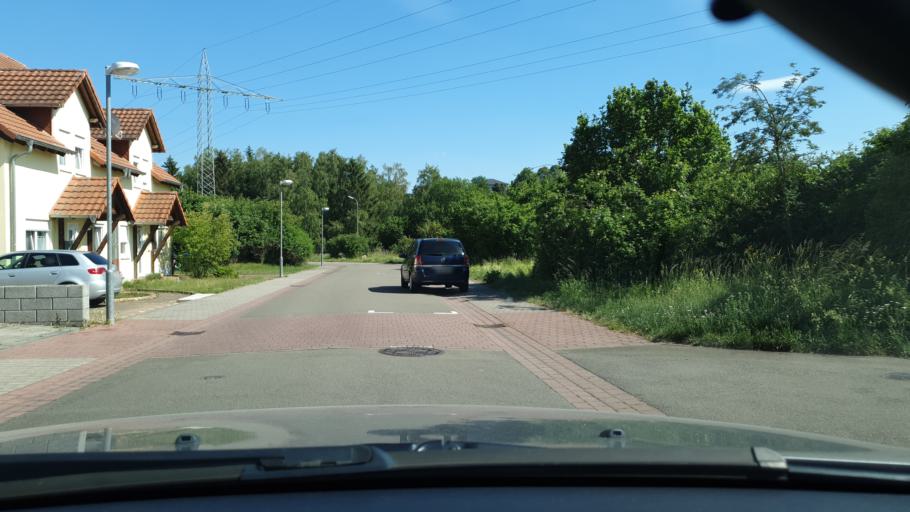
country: DE
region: Rheinland-Pfalz
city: Katzweiler
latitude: 49.4743
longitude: 7.6924
